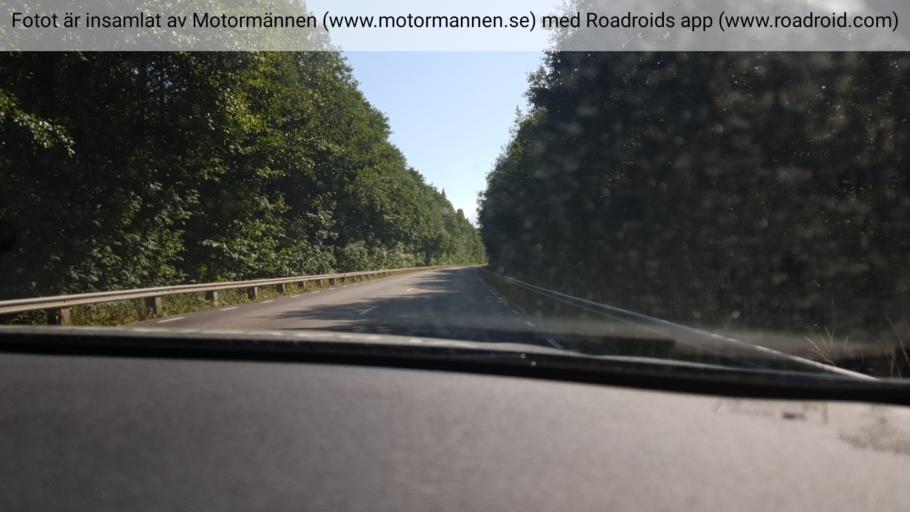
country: SE
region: Vaestra Goetaland
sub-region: Gotene Kommun
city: Kallby
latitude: 58.6059
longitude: 13.3980
